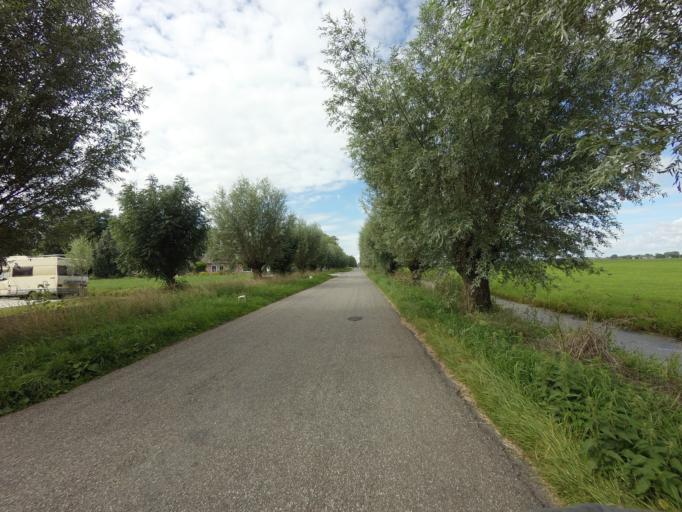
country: NL
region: Utrecht
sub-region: Gemeente Oudewater
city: Oudewater
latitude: 52.0100
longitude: 4.8698
